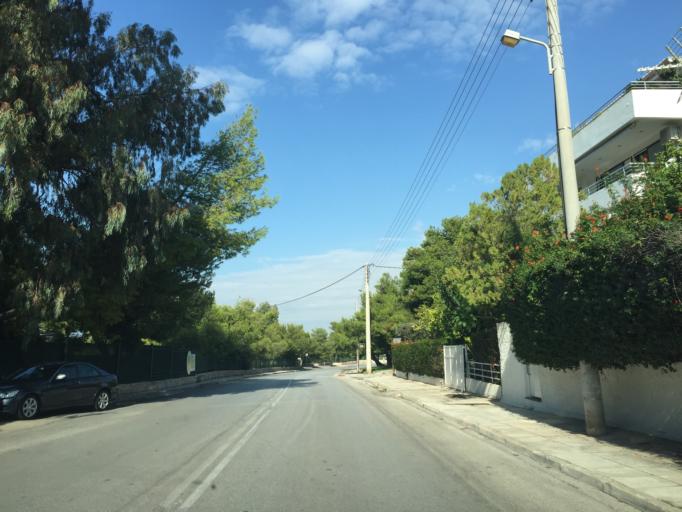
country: GR
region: Attica
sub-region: Nomarchia Anatolikis Attikis
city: Vouliagmeni
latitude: 37.8179
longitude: 23.7715
